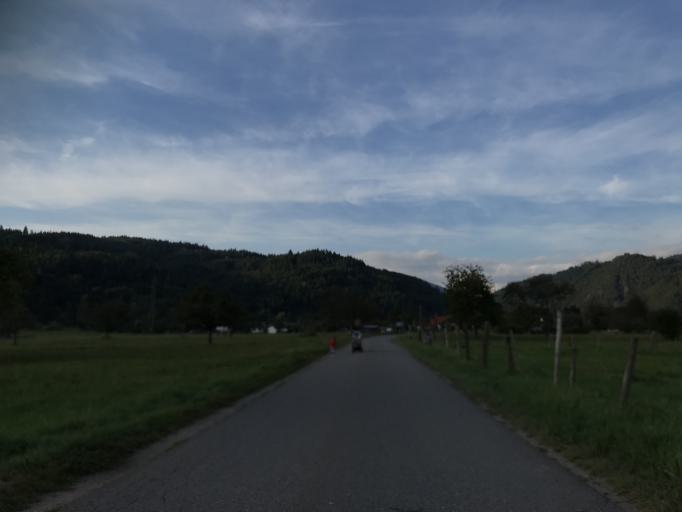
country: DE
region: Baden-Wuerttemberg
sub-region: Freiburg Region
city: Hausen
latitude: 47.6736
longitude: 7.8348
